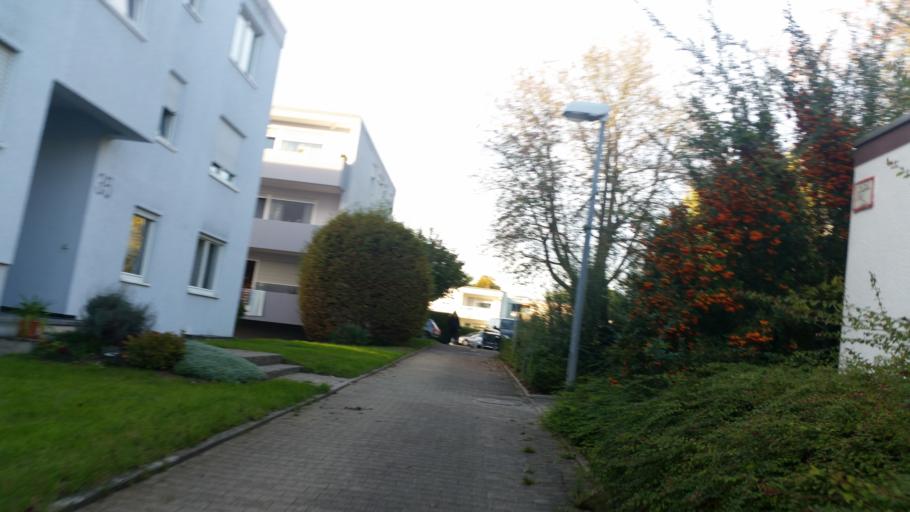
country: DE
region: Baden-Wuerttemberg
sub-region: Regierungsbezirk Stuttgart
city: Freiberg am Neckar
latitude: 48.9172
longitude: 9.2166
